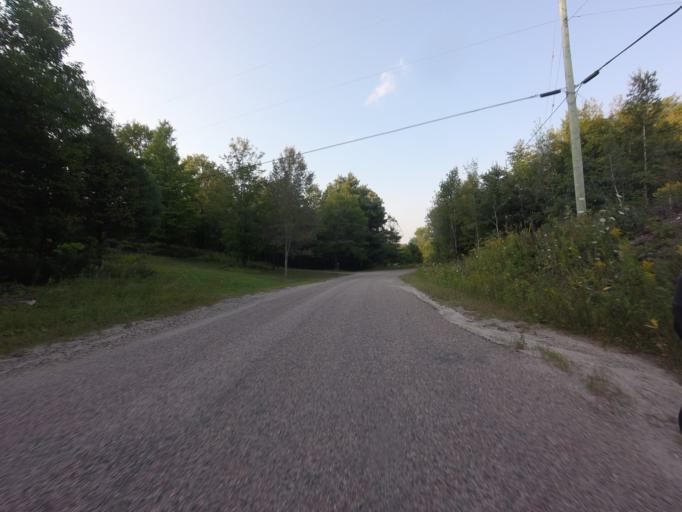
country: CA
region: Ontario
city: Renfrew
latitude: 45.0183
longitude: -76.7639
